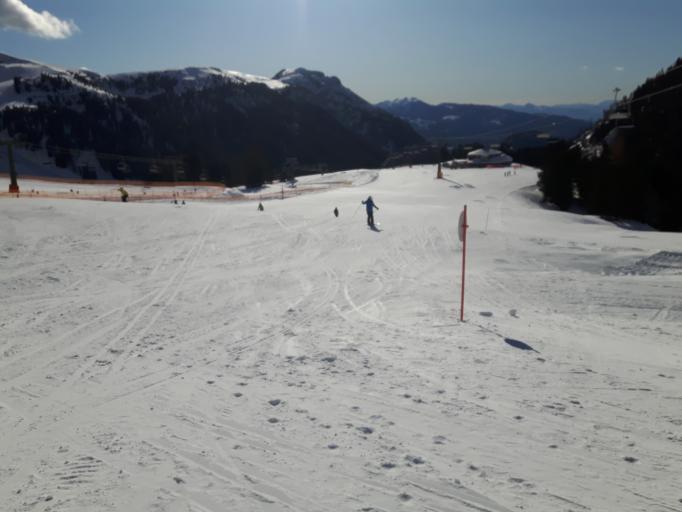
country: IT
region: Trentino-Alto Adige
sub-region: Provincia di Trento
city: Panchia
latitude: 46.3501
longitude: 11.5475
